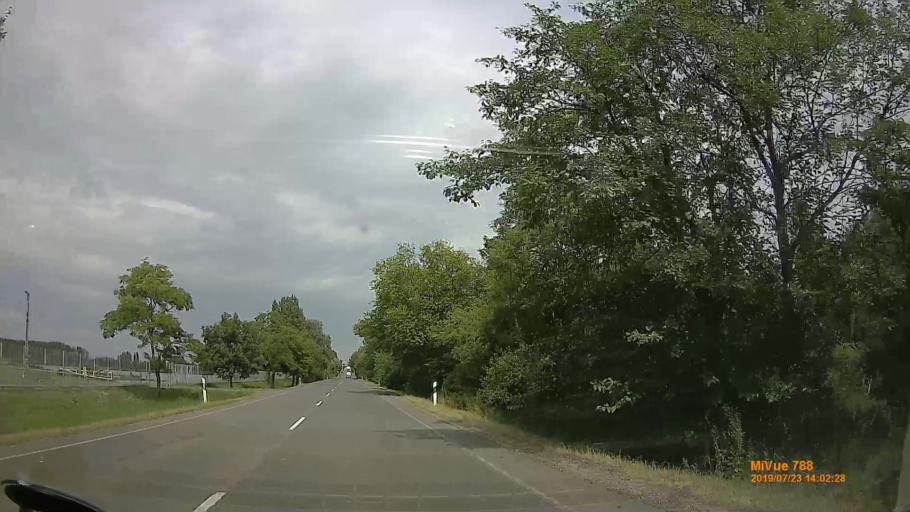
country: HU
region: Szabolcs-Szatmar-Bereg
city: Tiszavasvari
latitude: 47.9561
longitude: 21.3354
